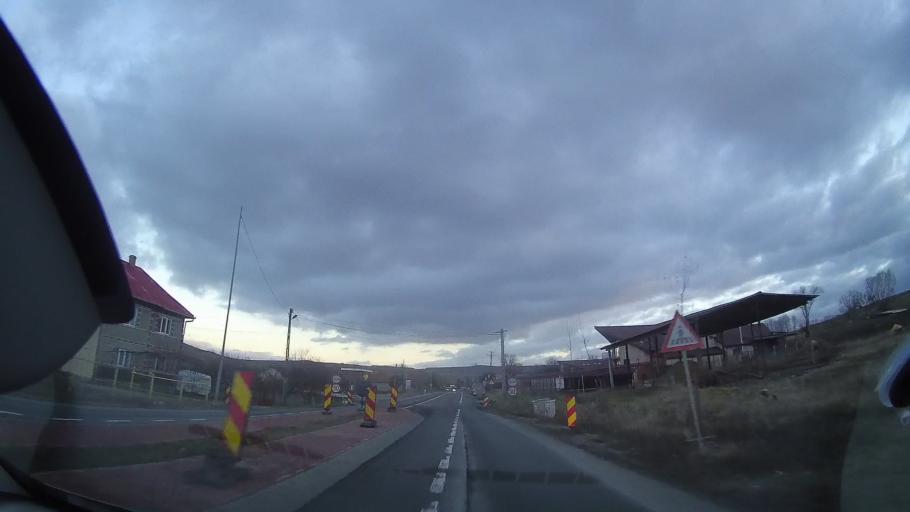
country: RO
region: Cluj
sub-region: Comuna Izvoru Crisului
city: Izvoru Crisului
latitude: 46.8170
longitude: 23.1761
